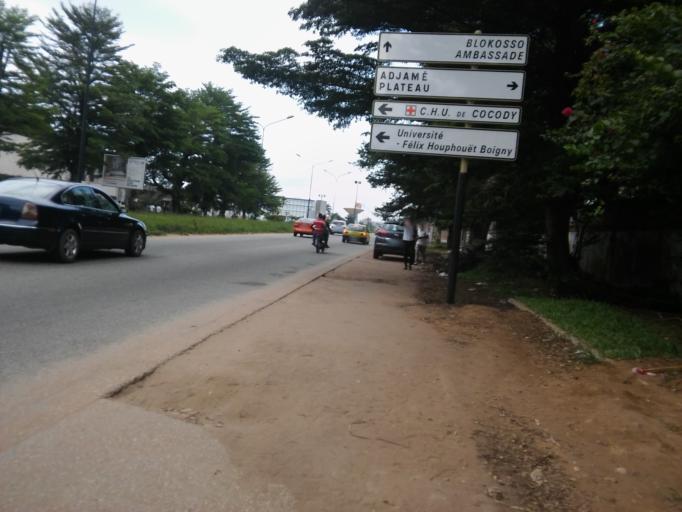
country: CI
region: Lagunes
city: Abidjan
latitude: 5.3462
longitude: -4.0028
